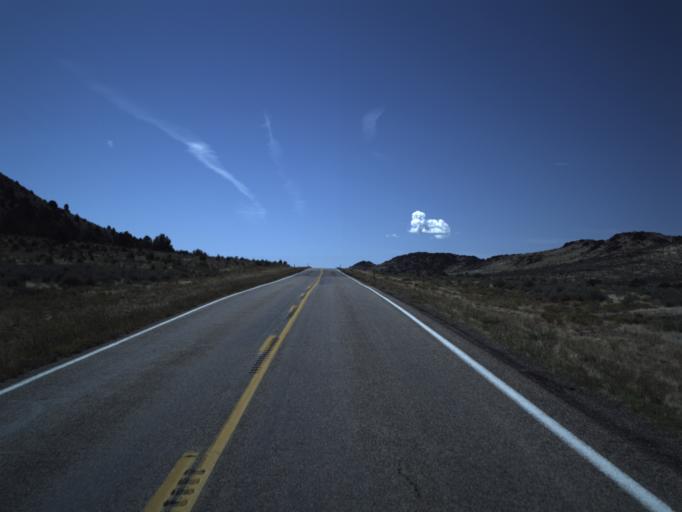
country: US
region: Utah
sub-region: Washington County
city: Enterprise
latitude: 37.3994
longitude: -113.6415
